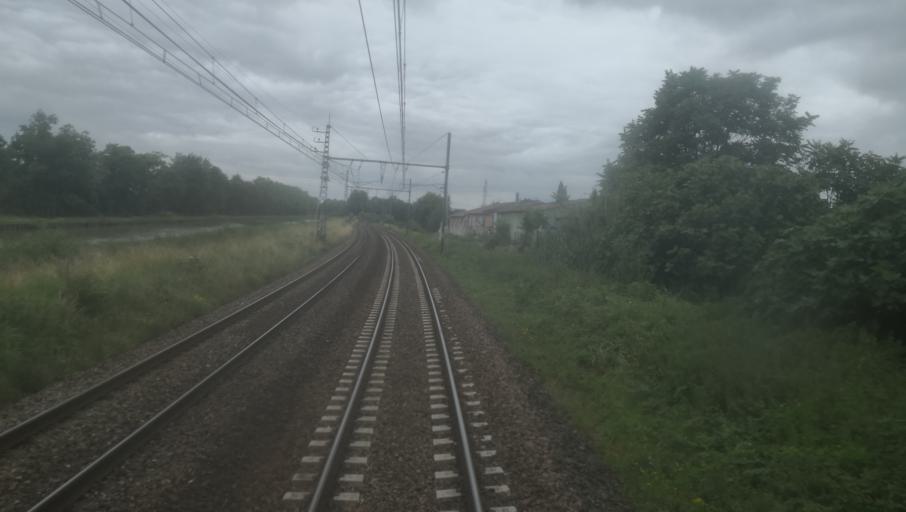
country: FR
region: Midi-Pyrenees
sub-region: Departement du Tarn-et-Garonne
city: Pompignan
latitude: 43.8174
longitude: 1.3102
